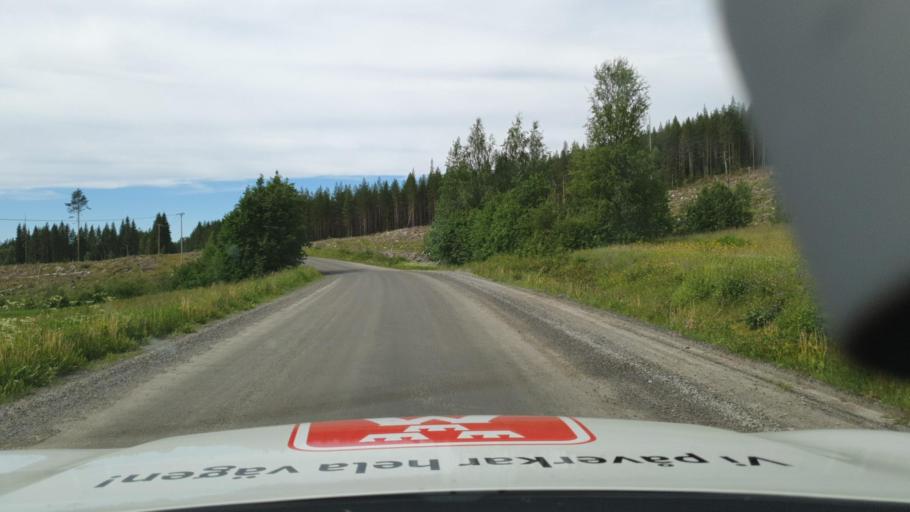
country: SE
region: Vaesterbotten
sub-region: Skelleftea Kommun
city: Burtraesk
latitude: 64.3844
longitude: 20.3123
